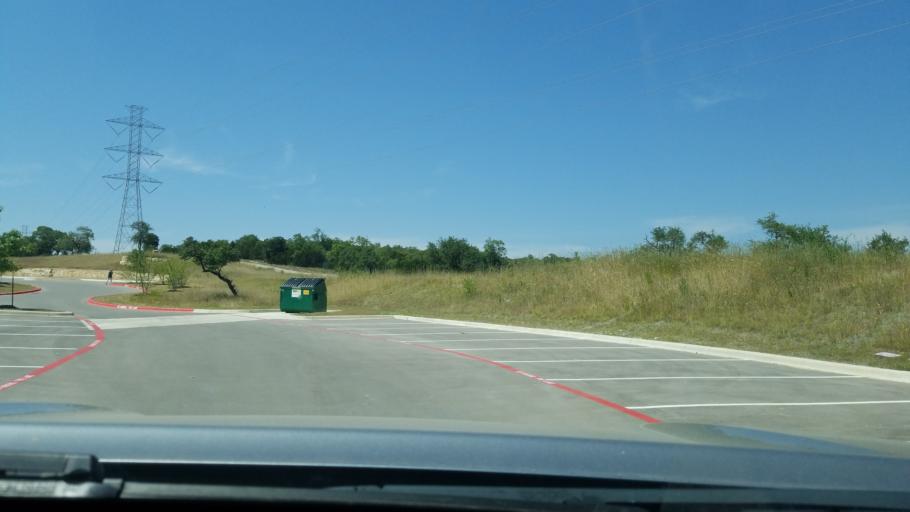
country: US
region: Texas
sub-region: Kendall County
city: Boerne
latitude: 29.8050
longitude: -98.6908
